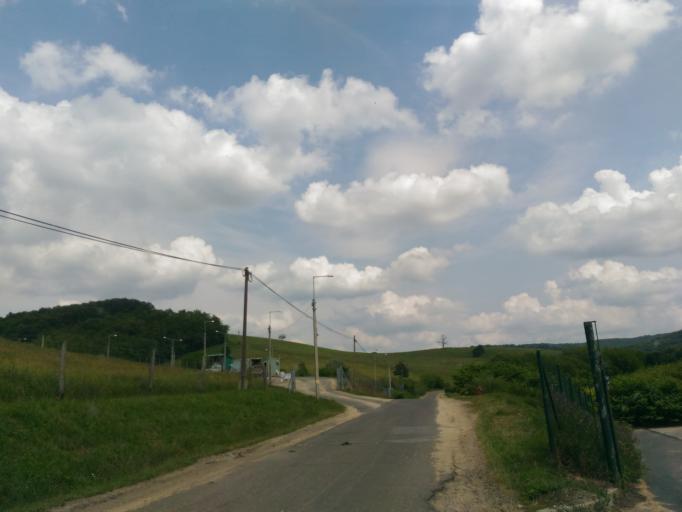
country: HU
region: Baranya
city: Komlo
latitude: 46.2149
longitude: 18.2580
